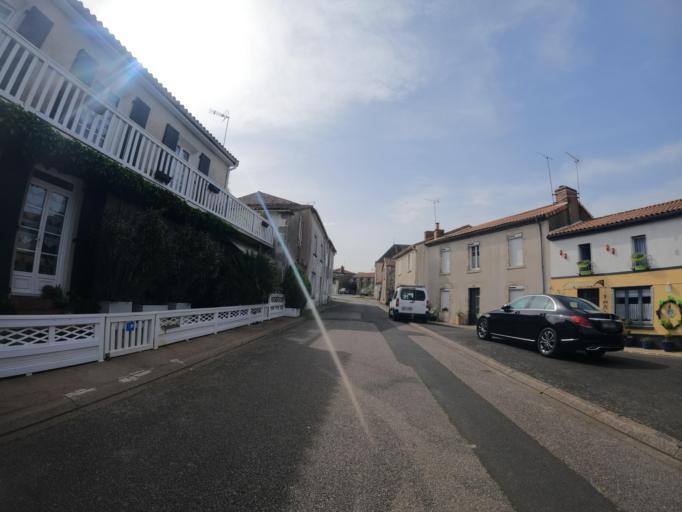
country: FR
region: Poitou-Charentes
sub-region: Departement des Deux-Sevres
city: La Chapelle-Saint-Laurent
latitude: 46.6942
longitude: -0.5009
